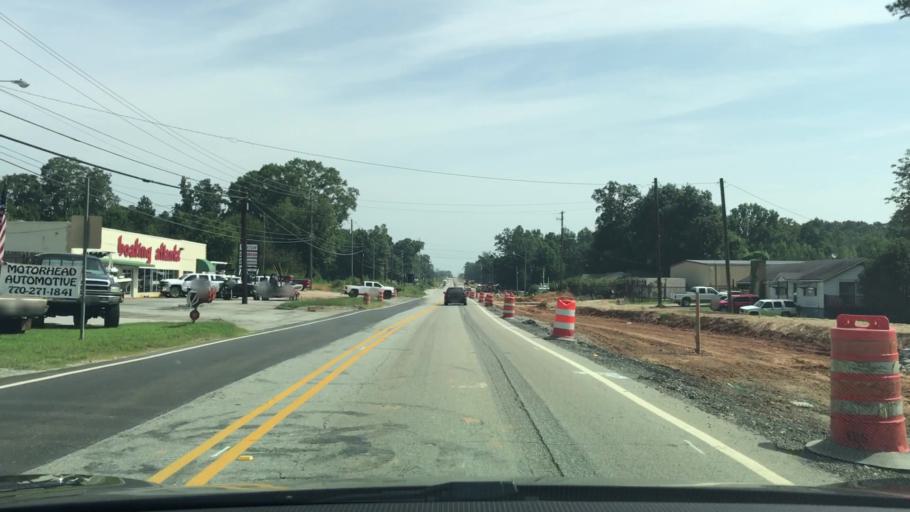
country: US
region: Georgia
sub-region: Gwinnett County
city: Buford
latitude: 34.1343
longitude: -83.9757
